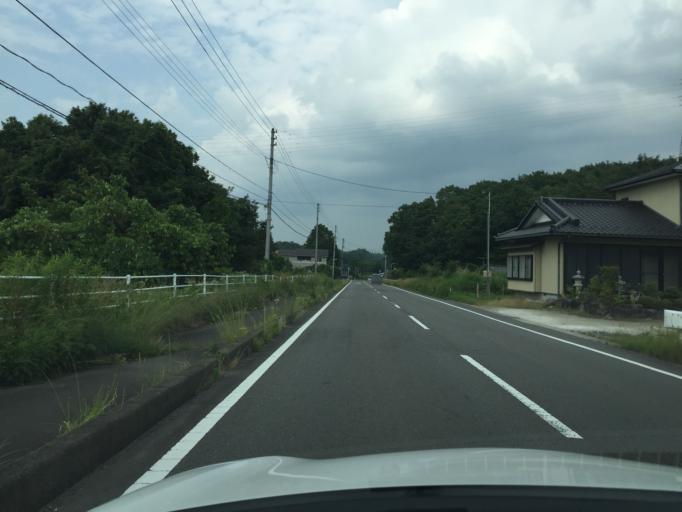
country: JP
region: Fukushima
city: Sukagawa
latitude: 37.2935
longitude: 140.4286
